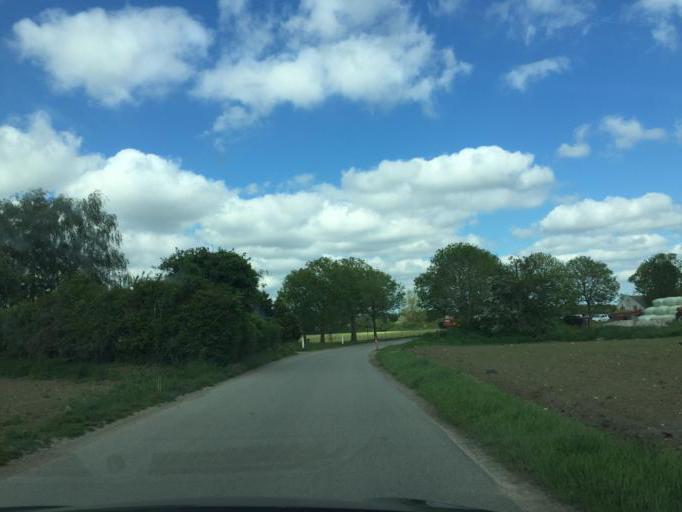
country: DK
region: South Denmark
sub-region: Odense Kommune
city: Bellinge
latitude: 55.3688
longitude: 10.2966
